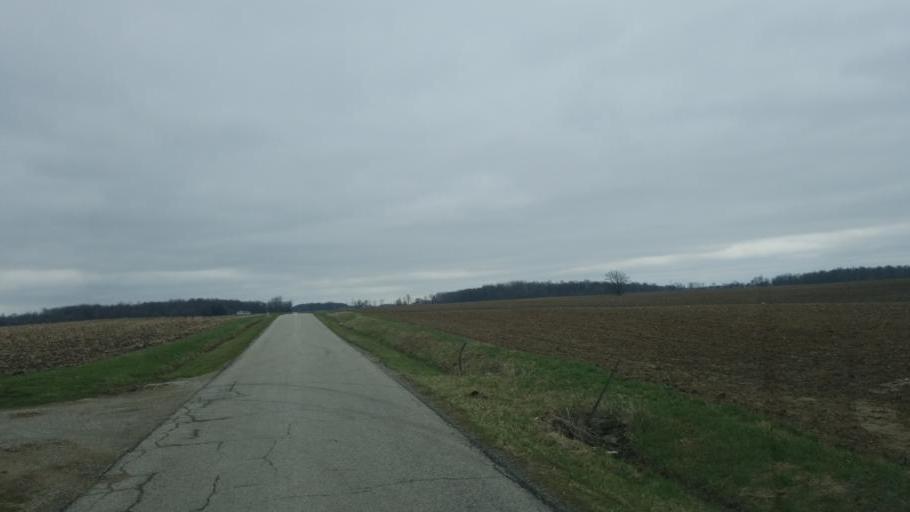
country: US
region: Ohio
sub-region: Crawford County
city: Bucyrus
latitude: 40.8559
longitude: -82.9929
